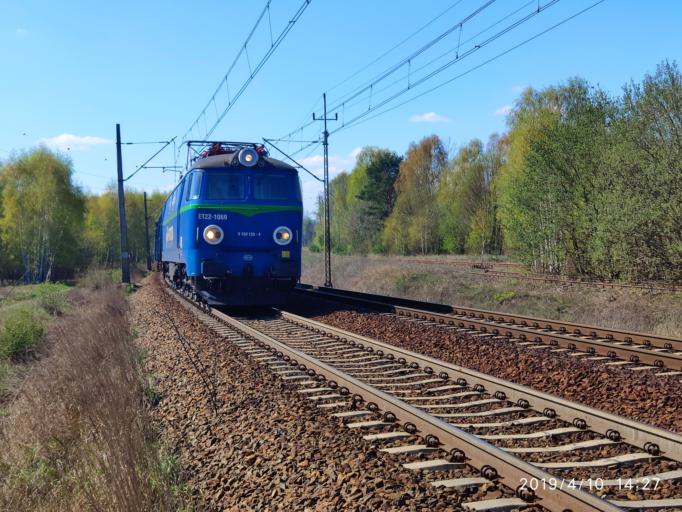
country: PL
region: Lubusz
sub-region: Zielona Gora
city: Zielona Gora
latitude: 51.9509
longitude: 15.4709
